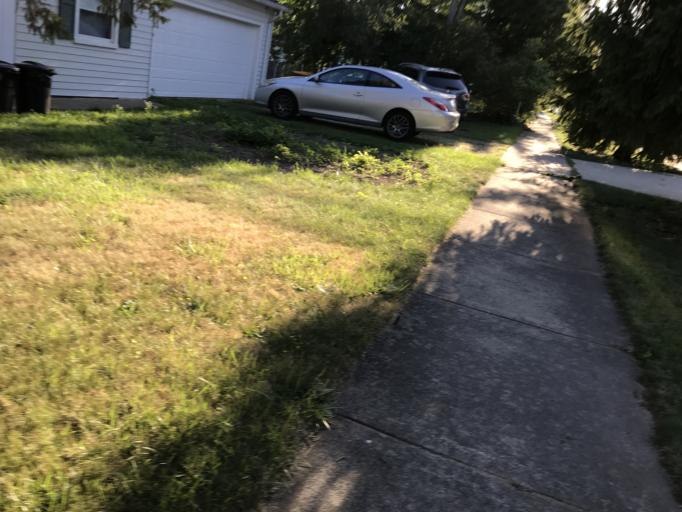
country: US
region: Michigan
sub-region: Oakland County
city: Farmington
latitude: 42.4579
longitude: -83.3520
